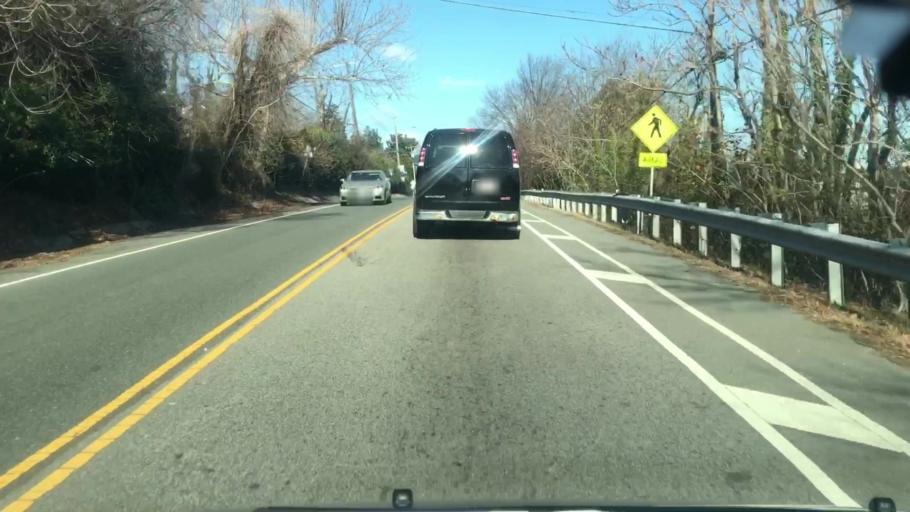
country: US
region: Virginia
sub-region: Fairfax County
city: Belle Haven
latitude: 38.7838
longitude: -77.0613
